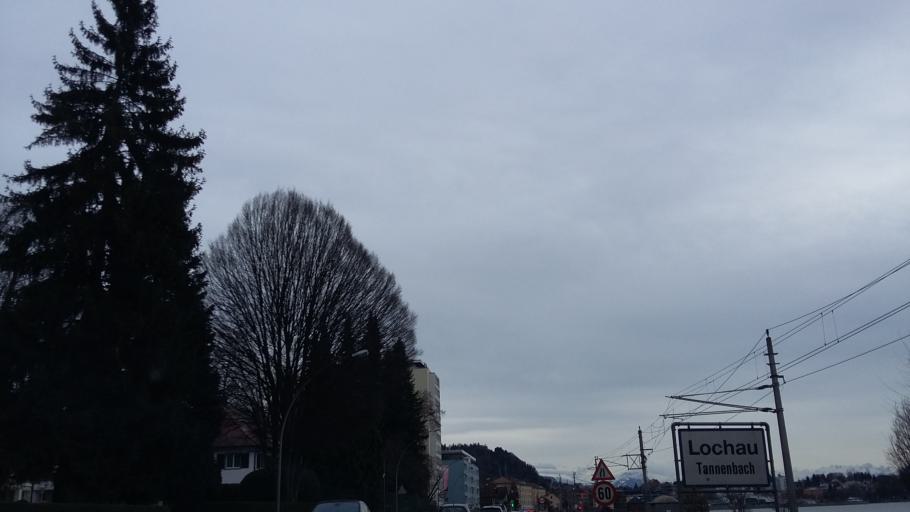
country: AT
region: Vorarlberg
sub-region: Politischer Bezirk Bregenz
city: Bregenz
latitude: 47.5147
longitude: 9.7540
